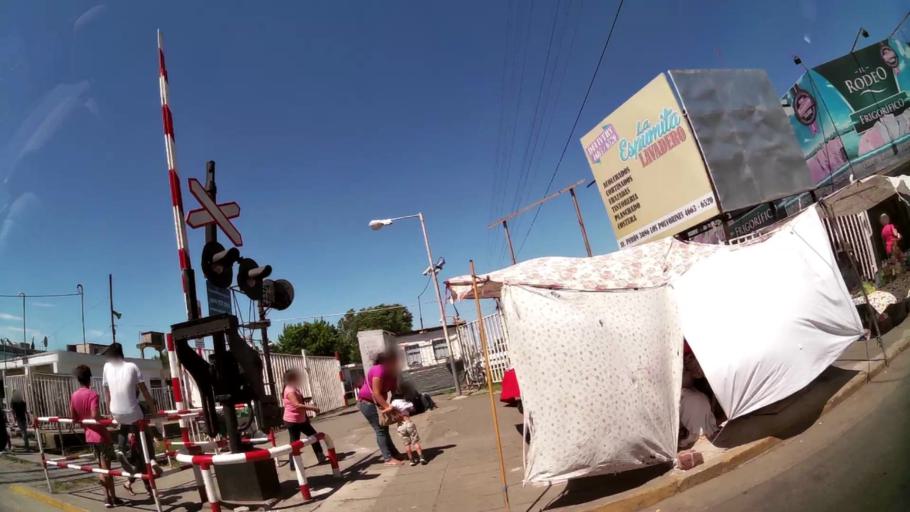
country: AR
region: Buenos Aires
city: Hurlingham
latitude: -34.5032
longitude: -58.6673
